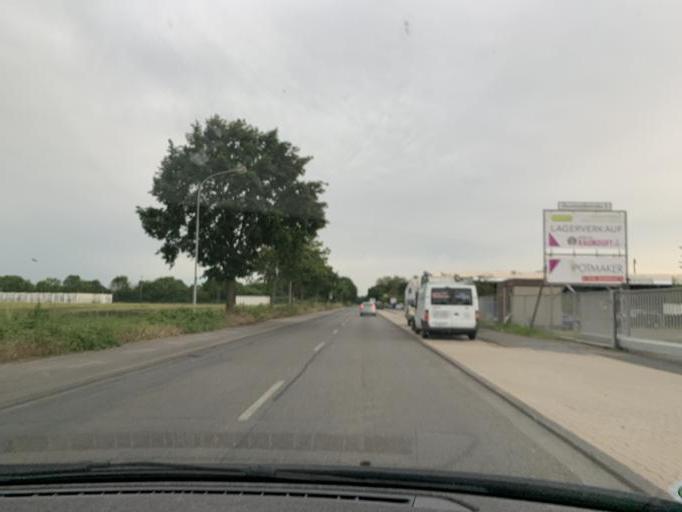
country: DE
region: North Rhine-Westphalia
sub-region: Regierungsbezirk Koln
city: Kerpen
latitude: 50.8788
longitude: 6.6811
